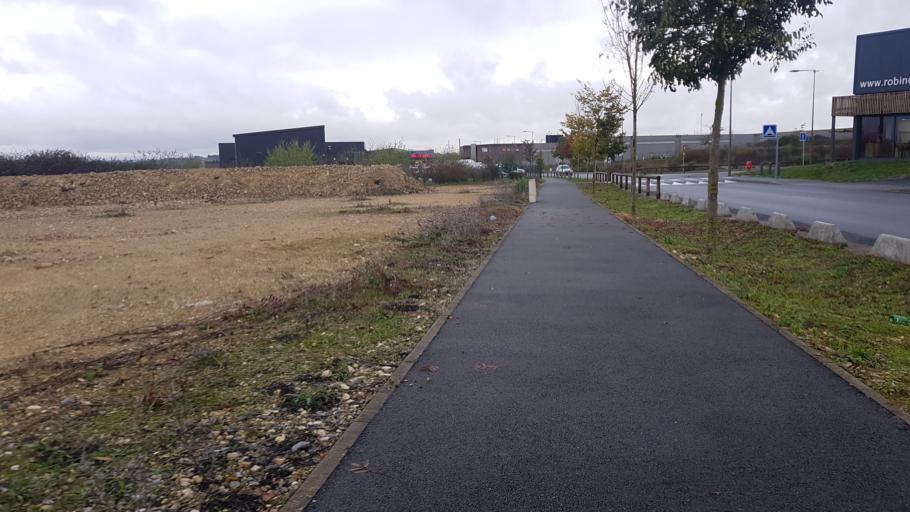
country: FR
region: Poitou-Charentes
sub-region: Departement de la Vienne
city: Chasseneuil-du-Poitou
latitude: 46.6513
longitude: 0.3601
